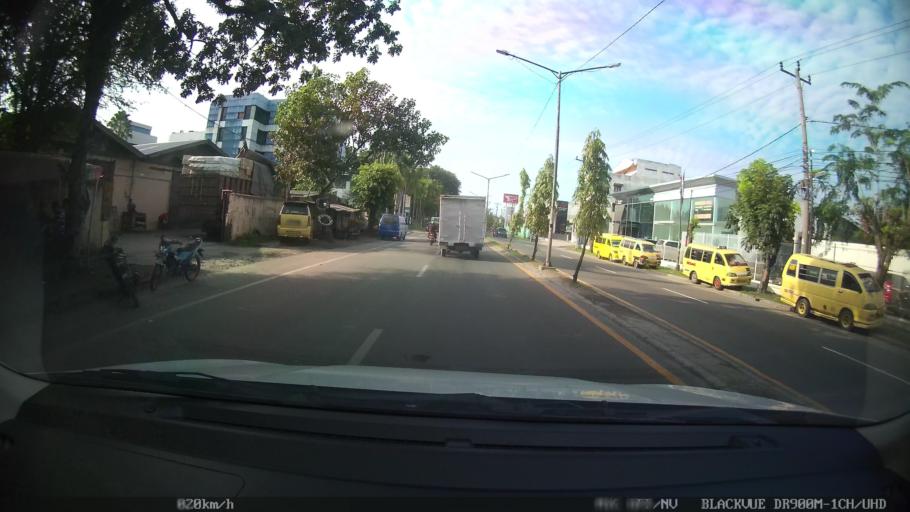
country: ID
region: North Sumatra
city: Medan
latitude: 3.6403
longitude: 98.6810
